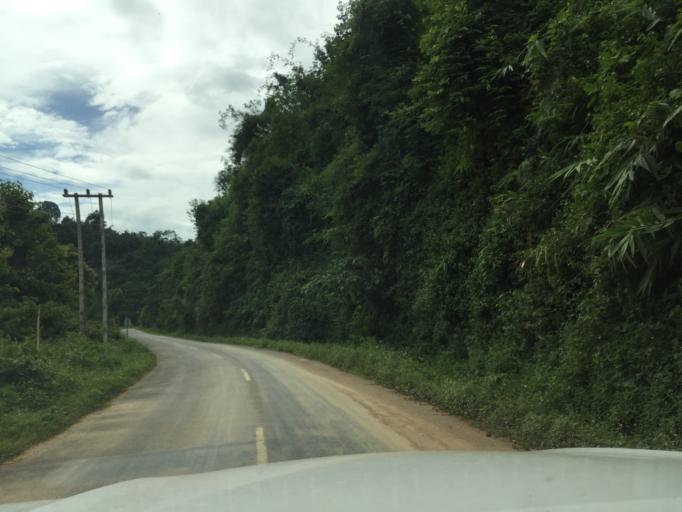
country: LA
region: Oudomxai
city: Muang La
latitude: 21.1048
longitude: 102.2344
